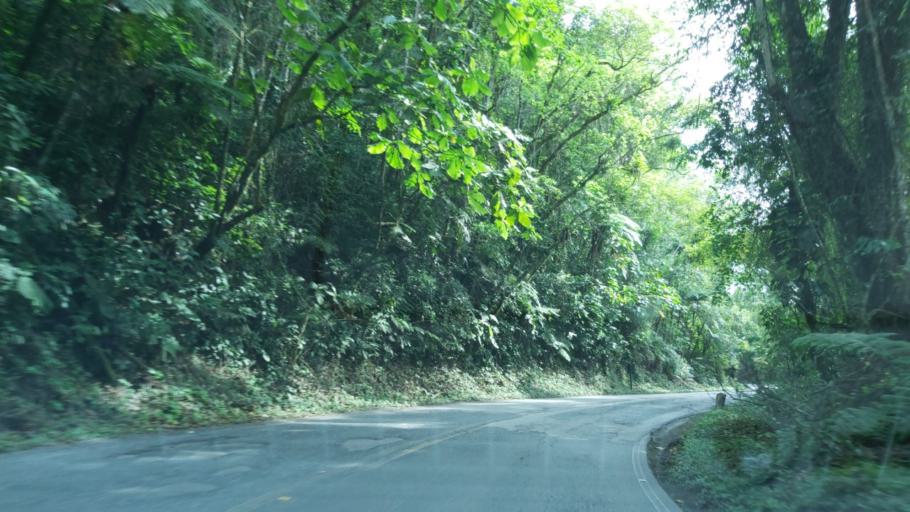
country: BR
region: Sao Paulo
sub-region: Juquia
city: Juquia
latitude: -24.0982
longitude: -47.6179
